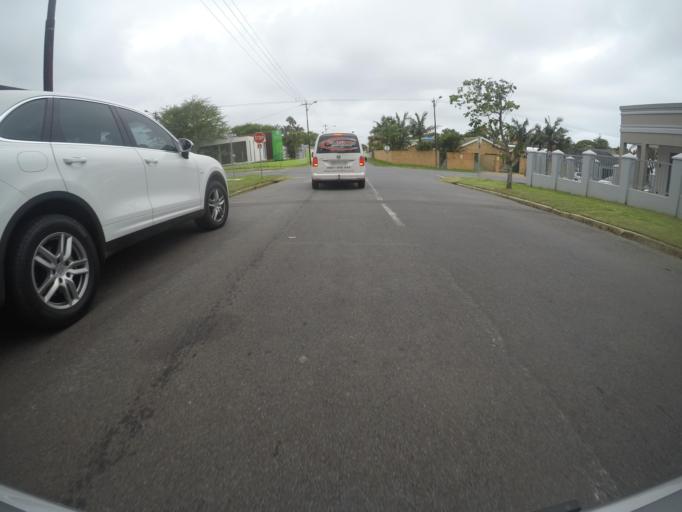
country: ZA
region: Eastern Cape
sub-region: Buffalo City Metropolitan Municipality
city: East London
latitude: -32.9812
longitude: 27.9045
